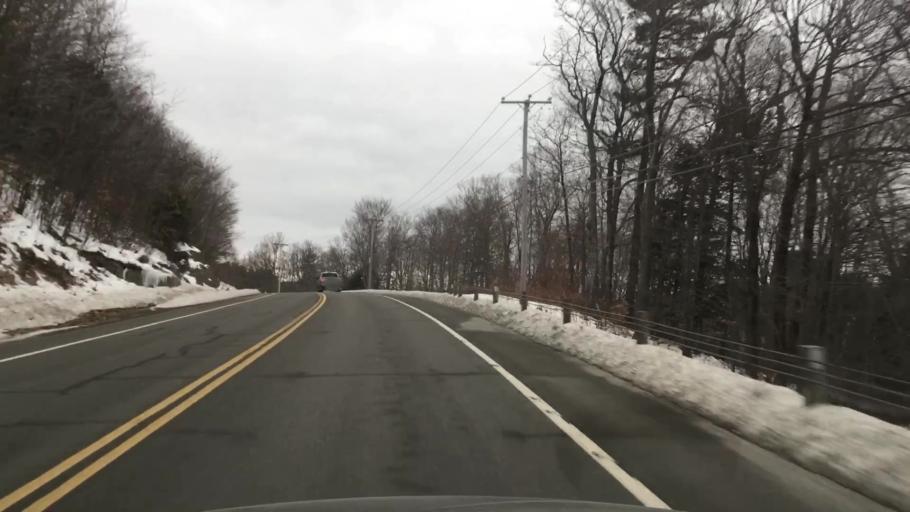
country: US
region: New Hampshire
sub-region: Merrimack County
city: Newbury
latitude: 43.3308
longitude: -72.0448
